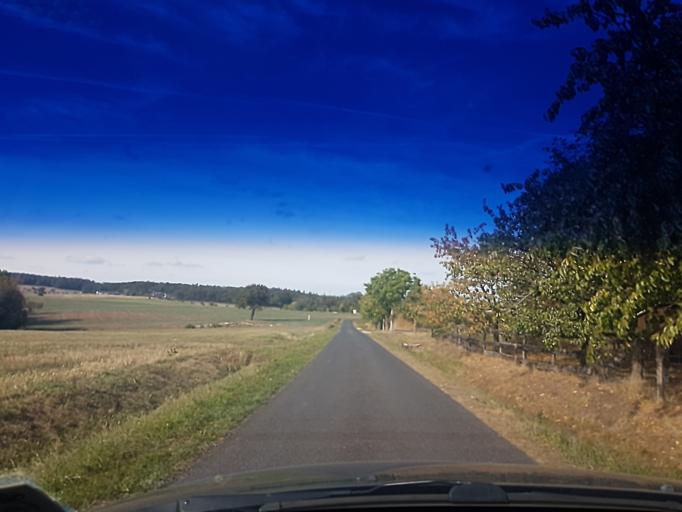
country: DE
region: Bavaria
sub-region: Regierungsbezirk Mittelfranken
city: Burghaslach
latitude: 49.7749
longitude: 10.5434
